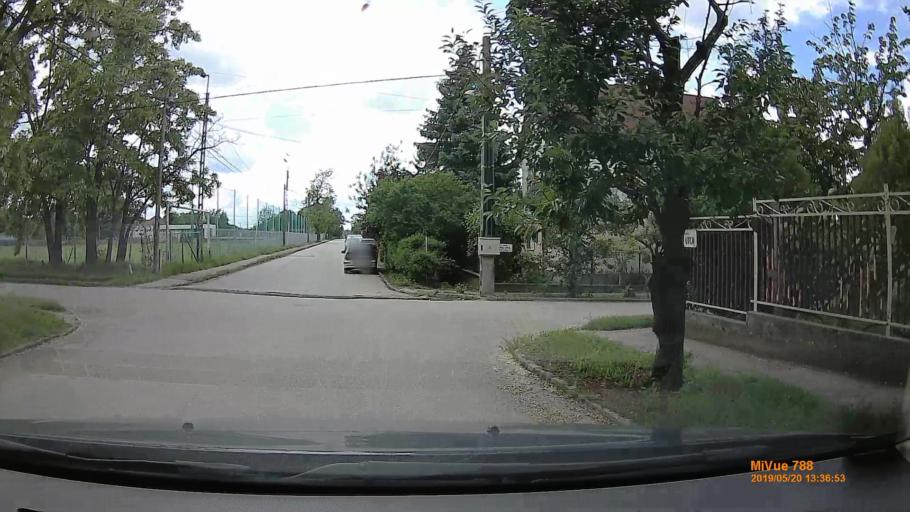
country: HU
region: Budapest
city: Budapest XVII. keruelet
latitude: 47.4784
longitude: 19.2976
